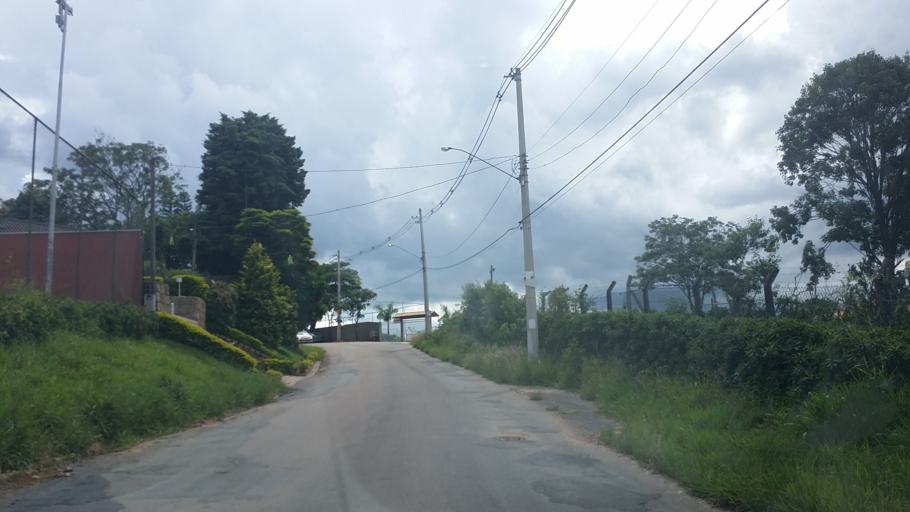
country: BR
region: Sao Paulo
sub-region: Itupeva
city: Itupeva
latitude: -23.1653
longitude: -47.0764
